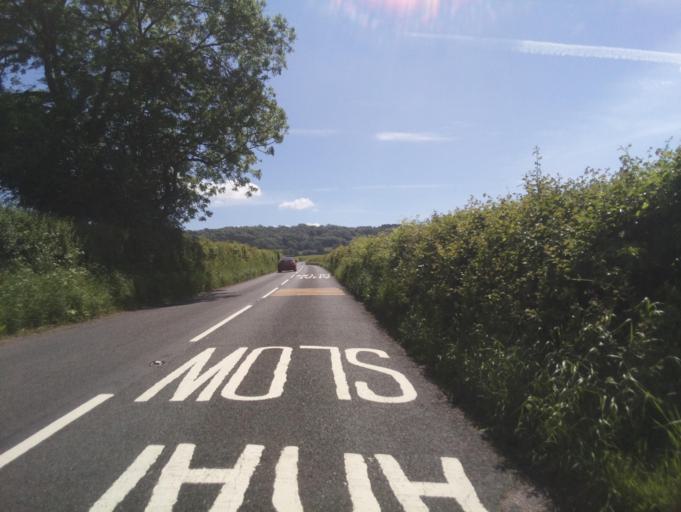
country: GB
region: Wales
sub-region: Monmouthshire
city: Monmouth
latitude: 51.7984
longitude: -2.7188
